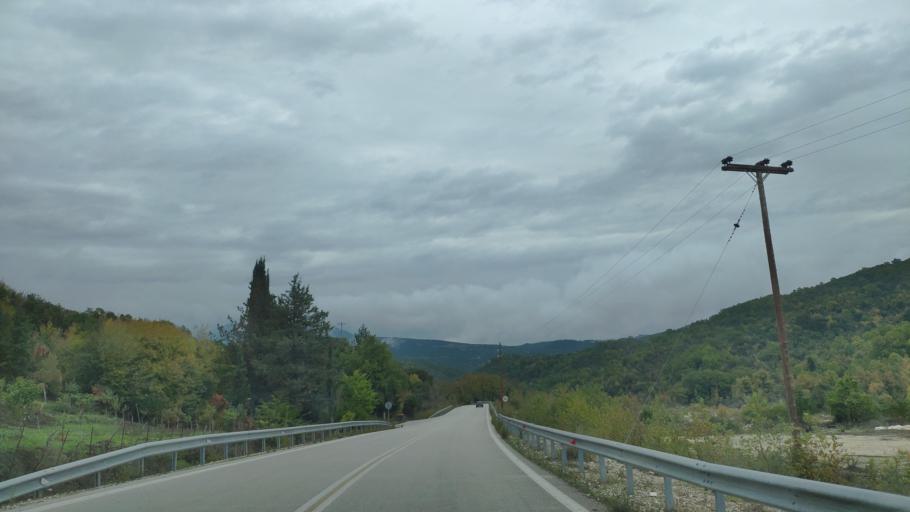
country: GR
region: Epirus
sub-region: Nomos Ioanninon
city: Pedini
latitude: 39.5246
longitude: 20.6934
